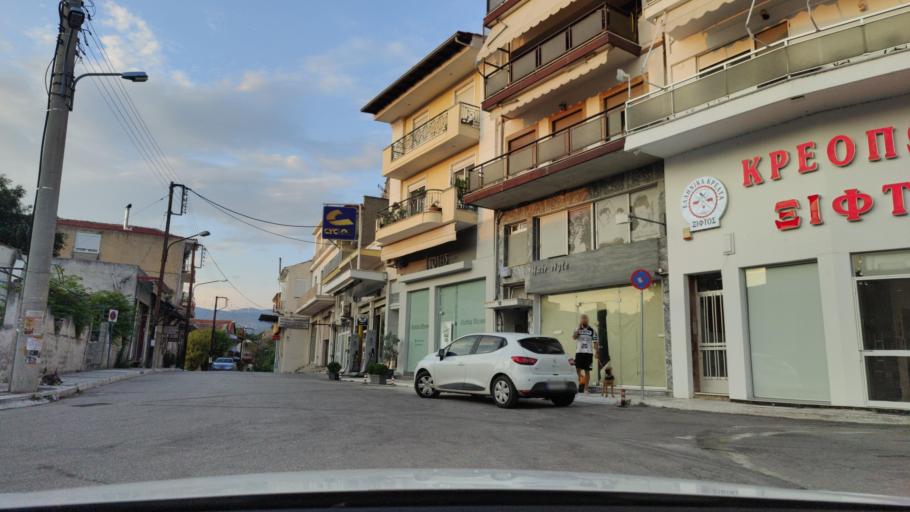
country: GR
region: Central Macedonia
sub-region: Nomos Serron
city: Sidirokastro
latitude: 41.2377
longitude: 23.3944
